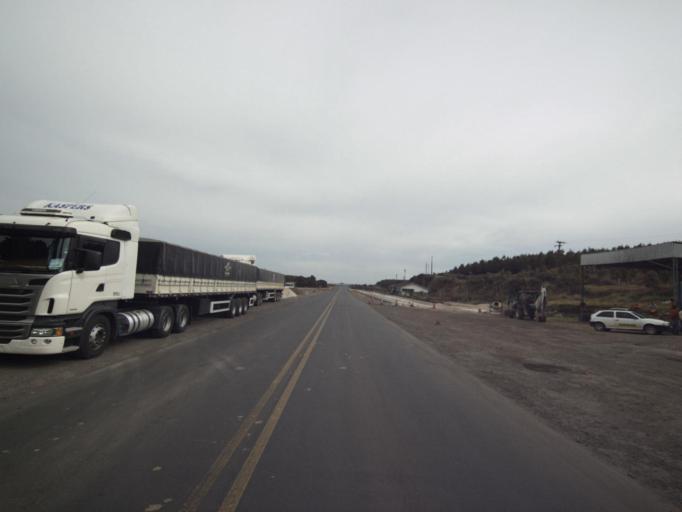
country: BR
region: Santa Catarina
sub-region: Cacador
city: Cacador
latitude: -26.6109
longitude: -51.4868
